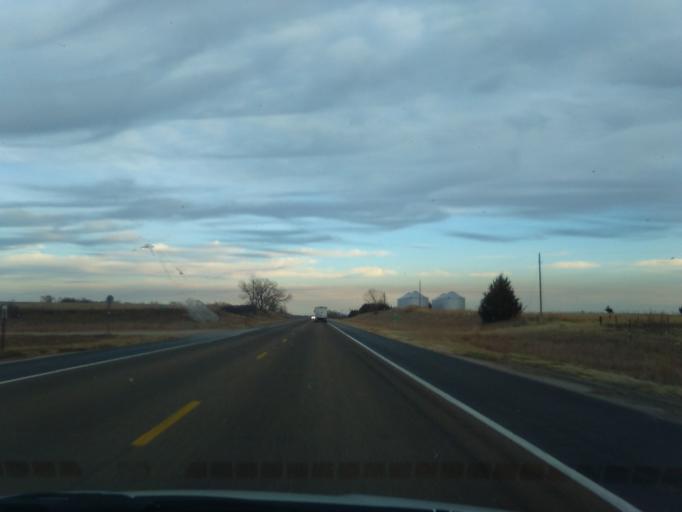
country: US
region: Nebraska
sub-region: Furnas County
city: Cambridge
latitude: 40.3073
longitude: -100.0430
